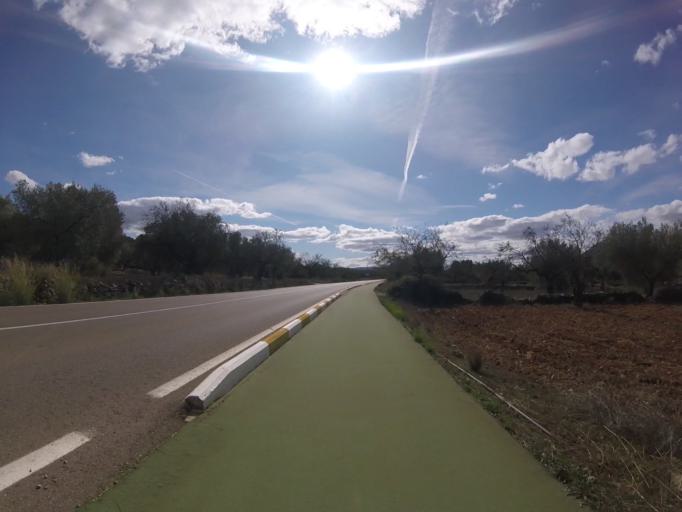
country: ES
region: Valencia
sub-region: Provincia de Castello
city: Cati
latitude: 40.4190
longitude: 0.0726
